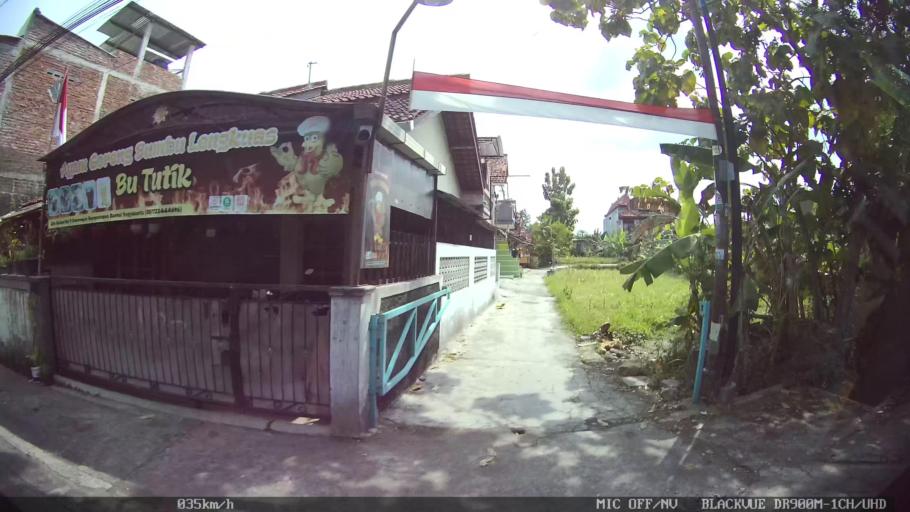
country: ID
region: Daerah Istimewa Yogyakarta
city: Depok
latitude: -7.7918
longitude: 110.4057
